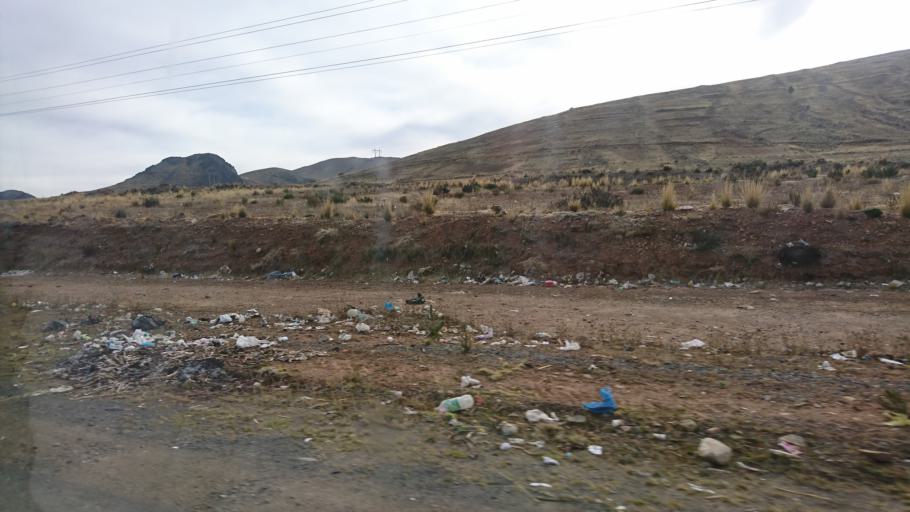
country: BO
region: La Paz
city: Batallas
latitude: -16.4101
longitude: -68.3496
